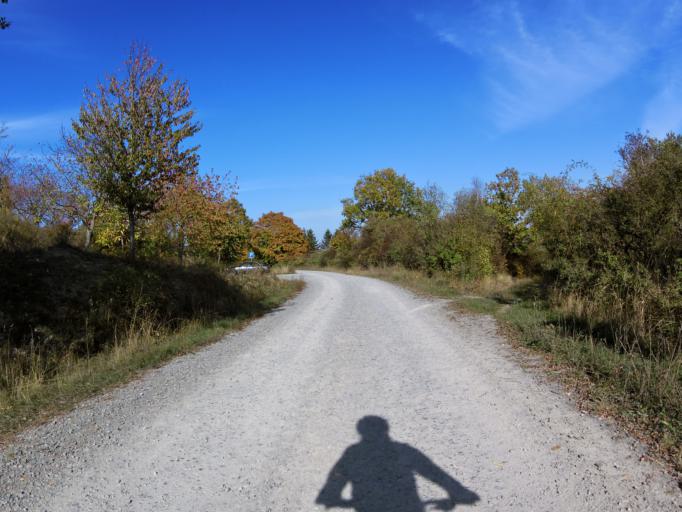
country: DE
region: Bavaria
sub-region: Regierungsbezirk Unterfranken
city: Eibelstadt
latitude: 49.7099
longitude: 9.9936
